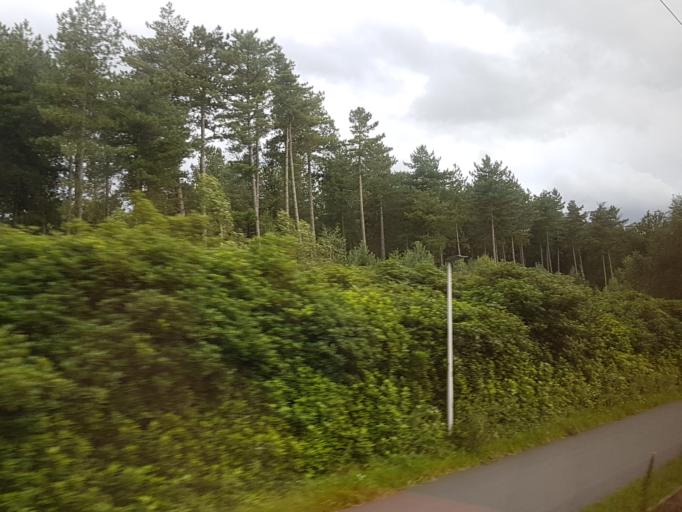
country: BE
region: Flanders
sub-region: Provincie Antwerpen
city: Kapellen
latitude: 51.3361
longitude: 4.4450
